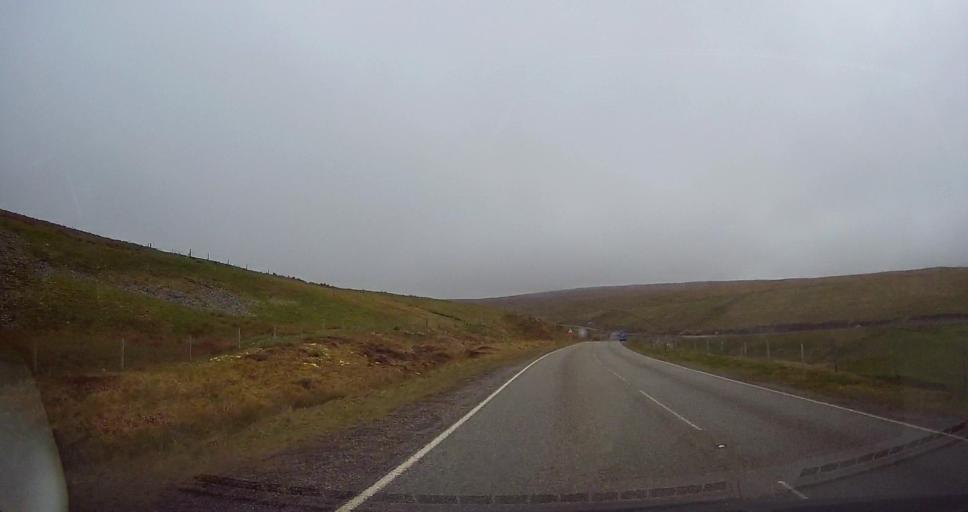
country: GB
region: Scotland
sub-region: Shetland Islands
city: Sandwick
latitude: 59.9863
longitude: -1.2791
